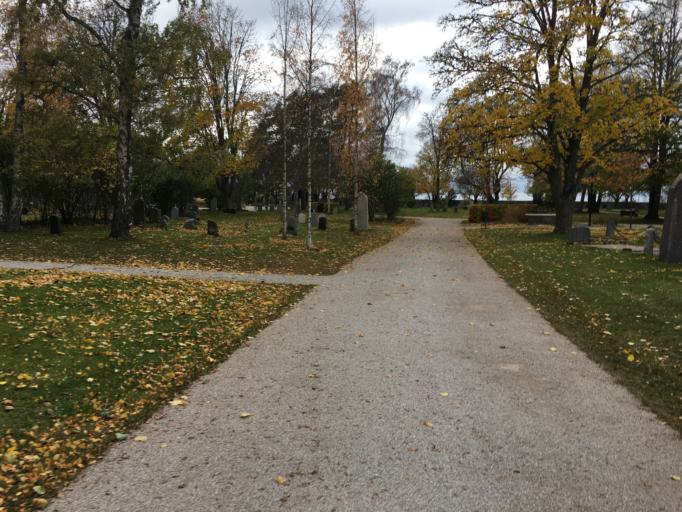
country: SE
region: Gotland
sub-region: Gotland
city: Visby
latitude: 57.6583
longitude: 18.3163
